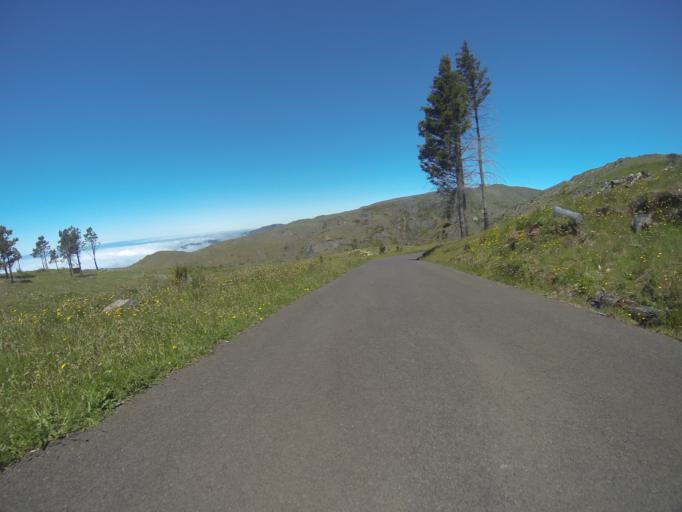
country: PT
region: Madeira
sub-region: Funchal
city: Nossa Senhora do Monte
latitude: 32.7076
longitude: -16.9132
